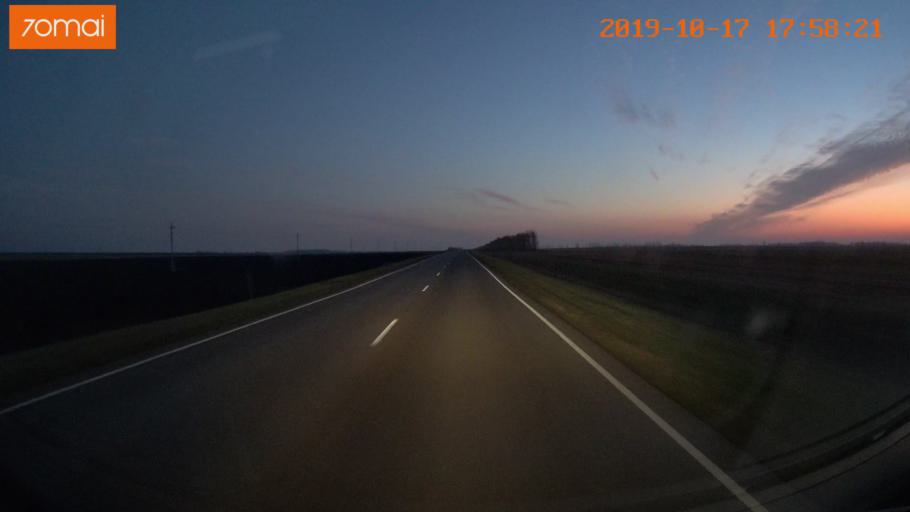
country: RU
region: Tula
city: Kurkino
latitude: 53.5565
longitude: 38.6288
